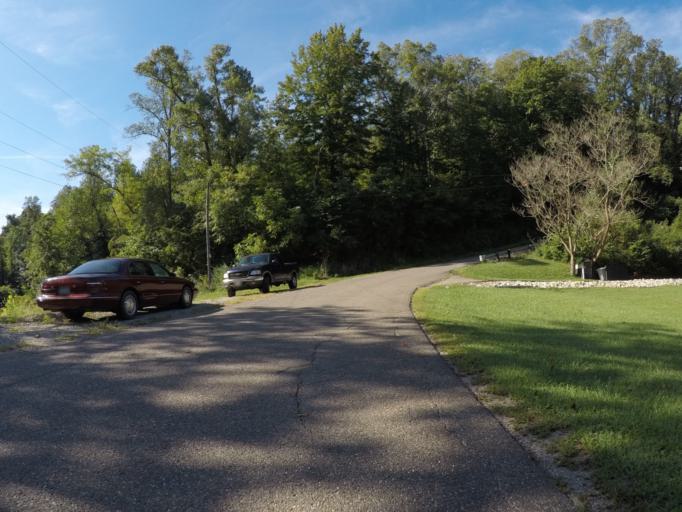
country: US
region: West Virginia
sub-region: Cabell County
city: Huntington
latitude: 38.4695
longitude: -82.4584
